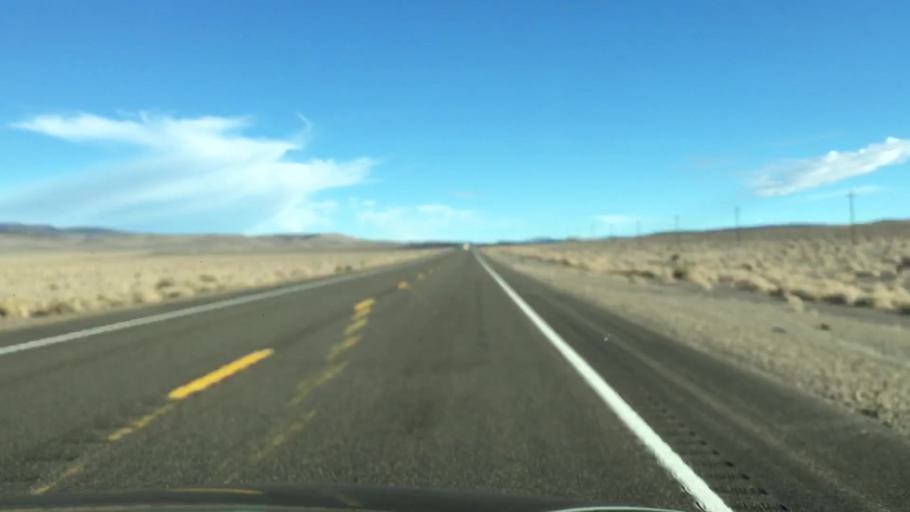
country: US
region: Nevada
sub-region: Mineral County
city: Hawthorne
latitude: 38.2526
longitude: -118.0768
